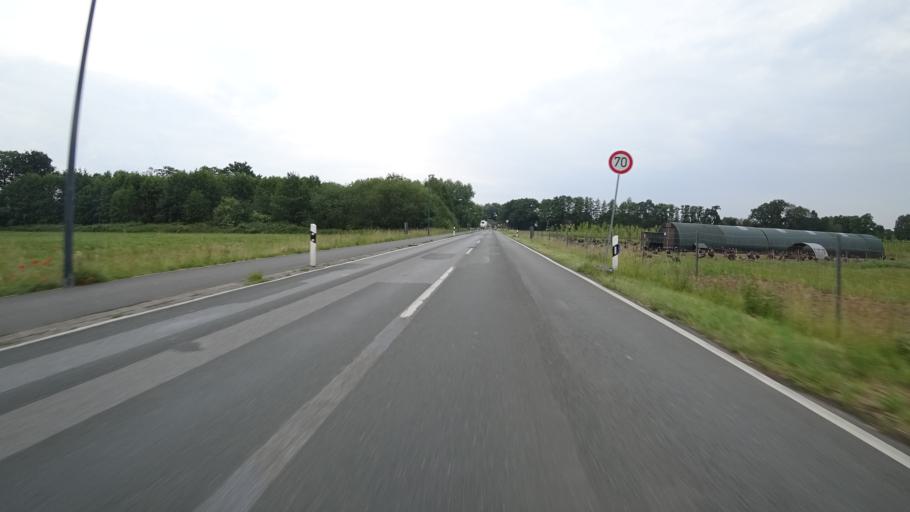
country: DE
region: North Rhine-Westphalia
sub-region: Regierungsbezirk Detmold
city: Guetersloh
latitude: 51.9244
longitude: 8.3722
